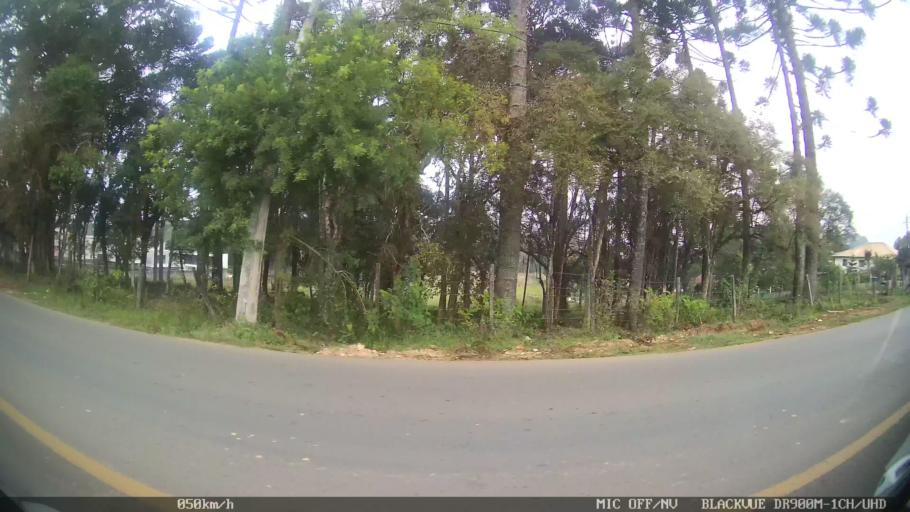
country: BR
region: Parana
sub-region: Almirante Tamandare
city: Almirante Tamandare
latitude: -25.3692
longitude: -49.3237
